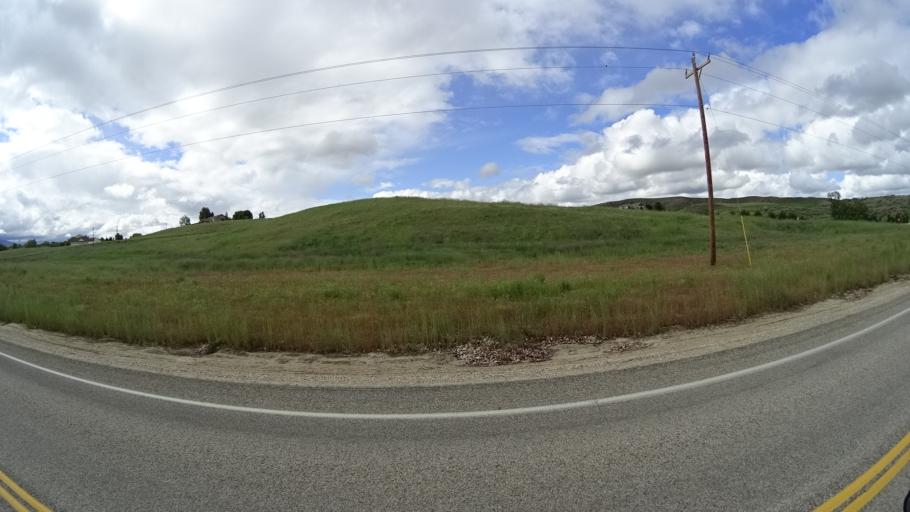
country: US
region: Idaho
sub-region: Ada County
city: Eagle
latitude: 43.7301
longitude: -116.2658
